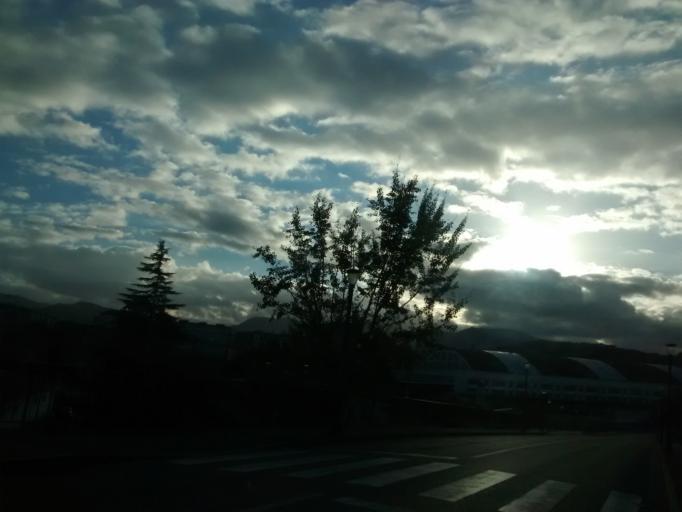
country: ES
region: Cantabria
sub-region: Provincia de Cantabria
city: Torrelavega
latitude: 43.3446
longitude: -4.0465
